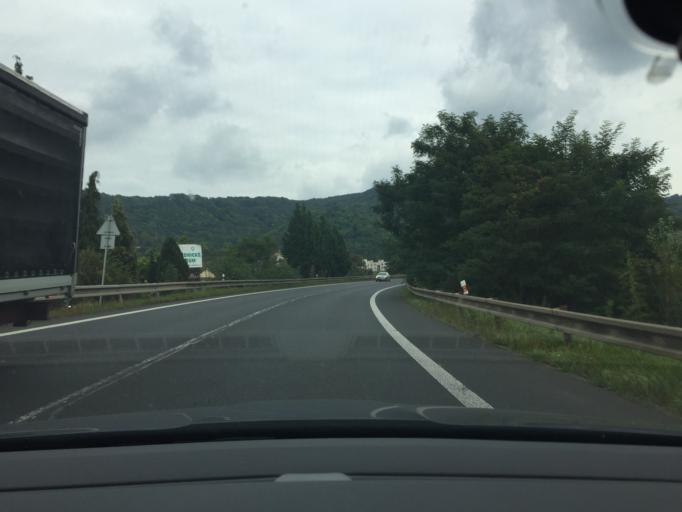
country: CZ
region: Ustecky
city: Velke Brezno
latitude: 50.6768
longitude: 14.1113
